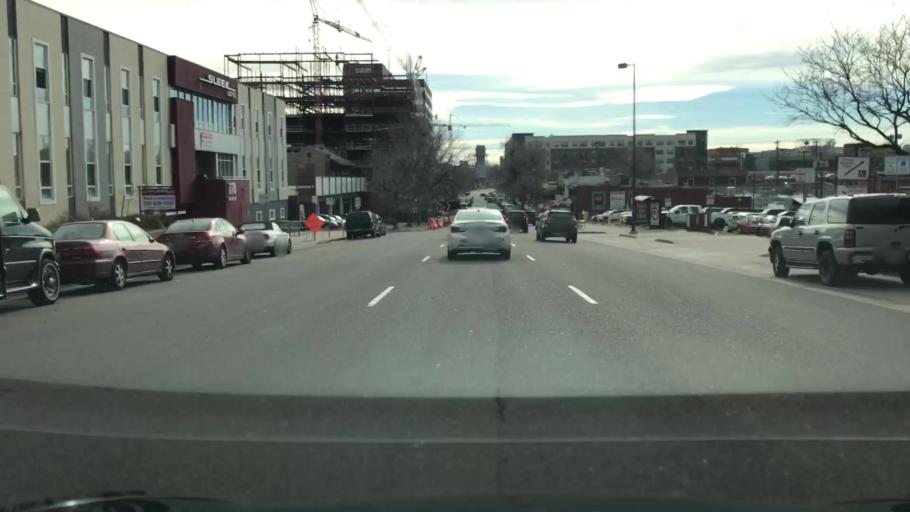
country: US
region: Colorado
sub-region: Denver County
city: Denver
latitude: 39.7287
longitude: -104.9836
